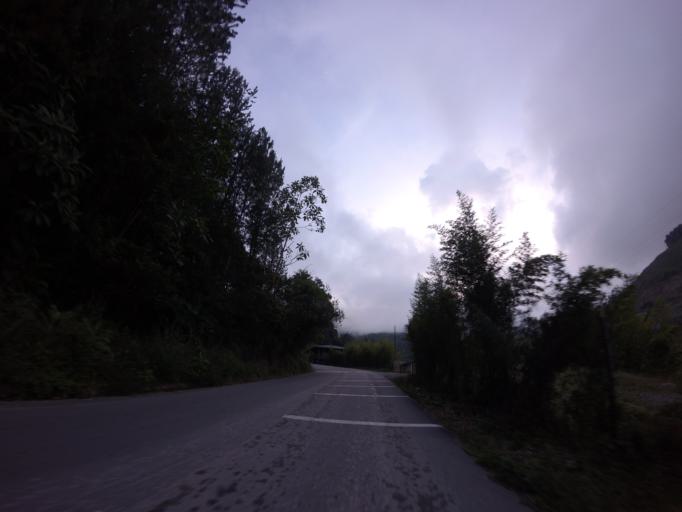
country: CO
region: Caldas
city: Manzanares
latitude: 5.2861
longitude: -75.1500
